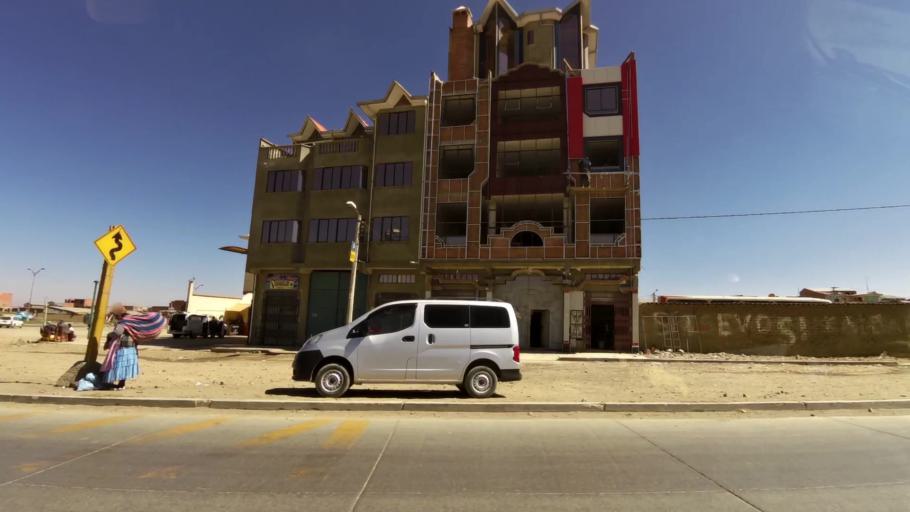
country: BO
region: La Paz
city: La Paz
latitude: -16.5092
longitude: -68.2131
